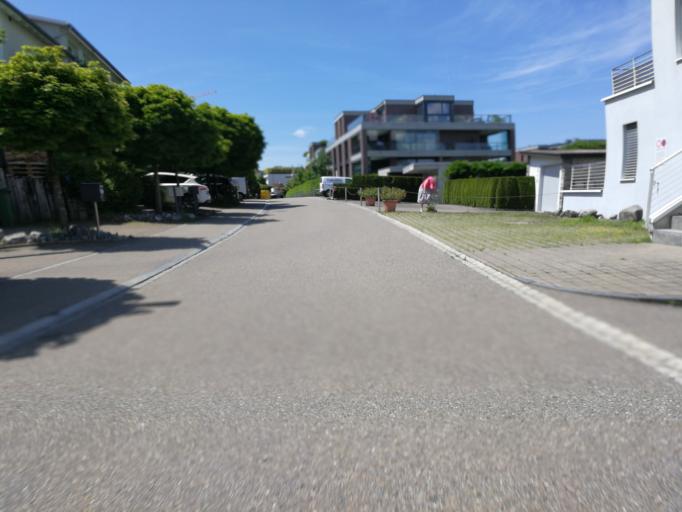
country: CH
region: Schwyz
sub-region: Bezirk Hoefe
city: Freienbach
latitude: 47.2014
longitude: 8.7739
